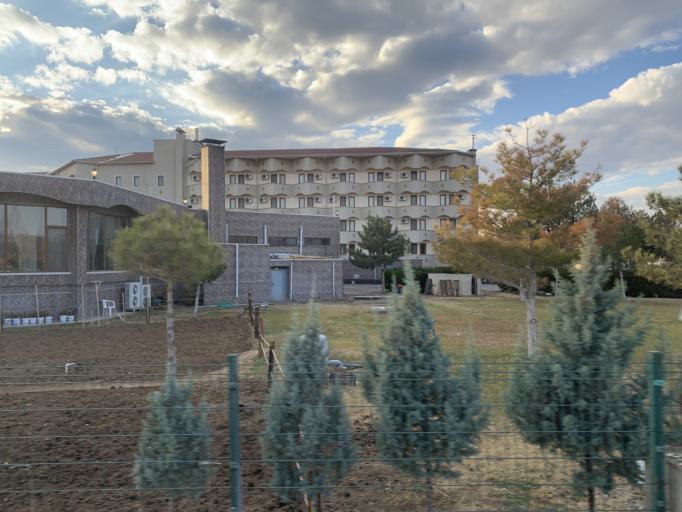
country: TR
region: Nevsehir
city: Avanos
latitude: 38.7029
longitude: 34.8387
